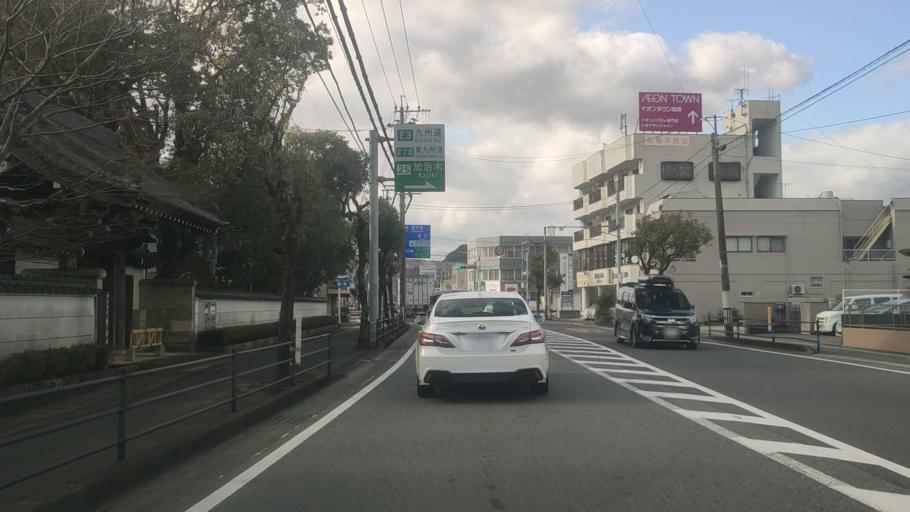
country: JP
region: Kagoshima
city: Kajiki
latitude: 31.7344
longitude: 130.6687
